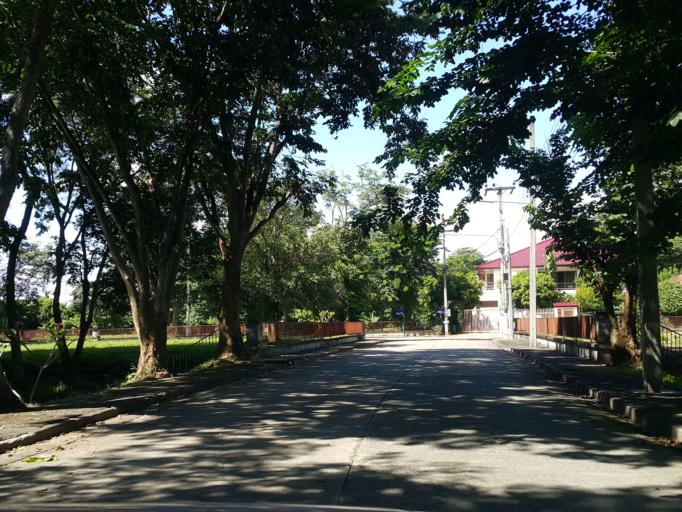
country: TH
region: Chiang Mai
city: San Sai
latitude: 18.8495
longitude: 99.0035
